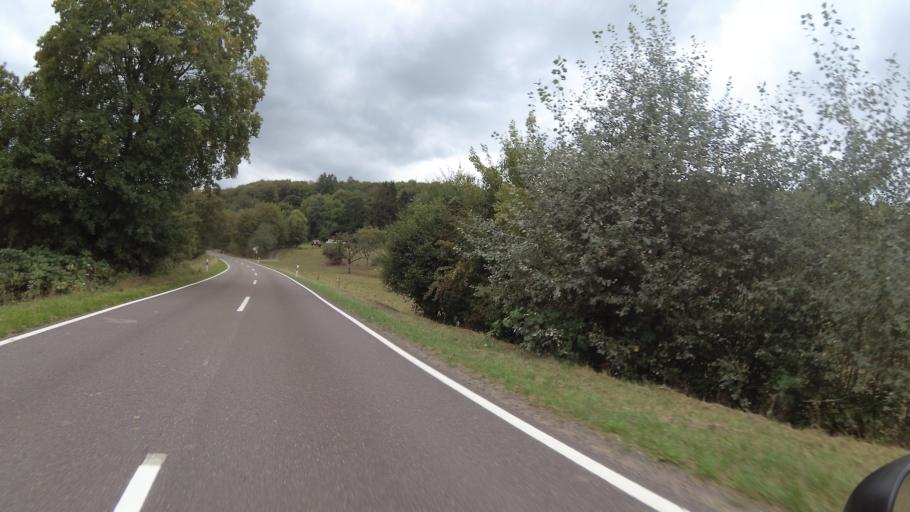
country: FR
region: Lorraine
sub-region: Departement de la Moselle
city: Sarreguemines
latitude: 49.1503
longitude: 7.0797
